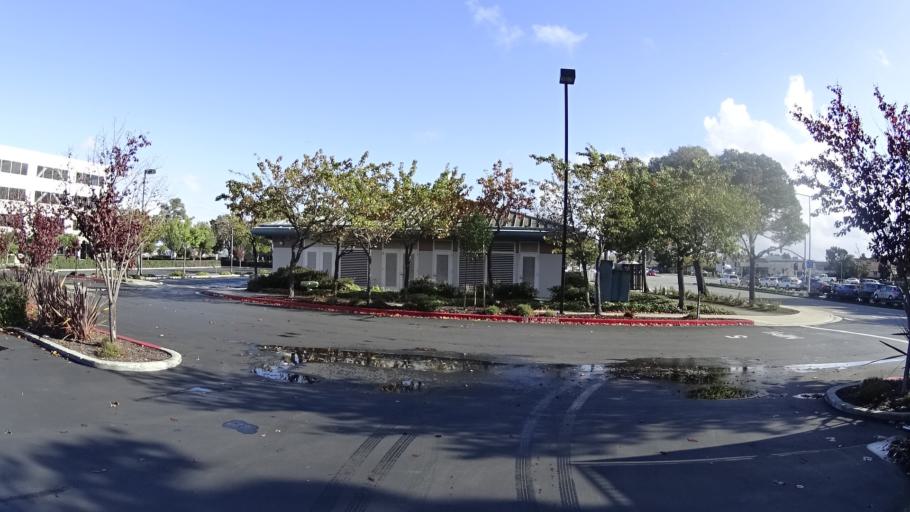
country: US
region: California
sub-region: San Mateo County
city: Foster City
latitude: 37.5553
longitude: -122.2780
